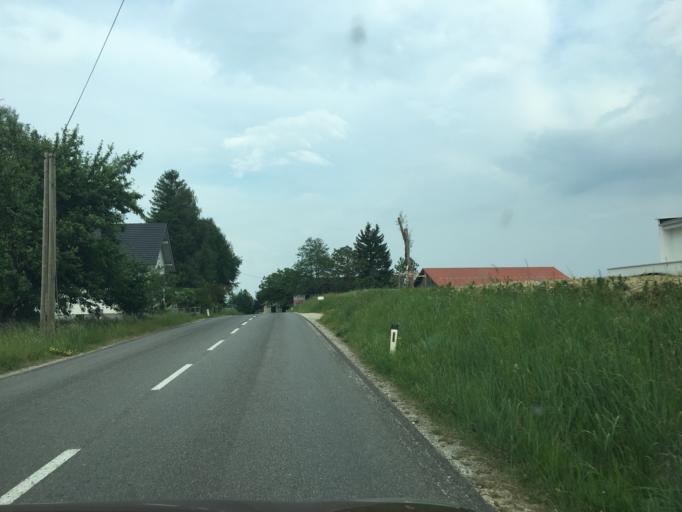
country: AT
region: Upper Austria
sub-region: Politischer Bezirk Ried im Innkreis
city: Waldzell
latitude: 48.1239
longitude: 13.3765
